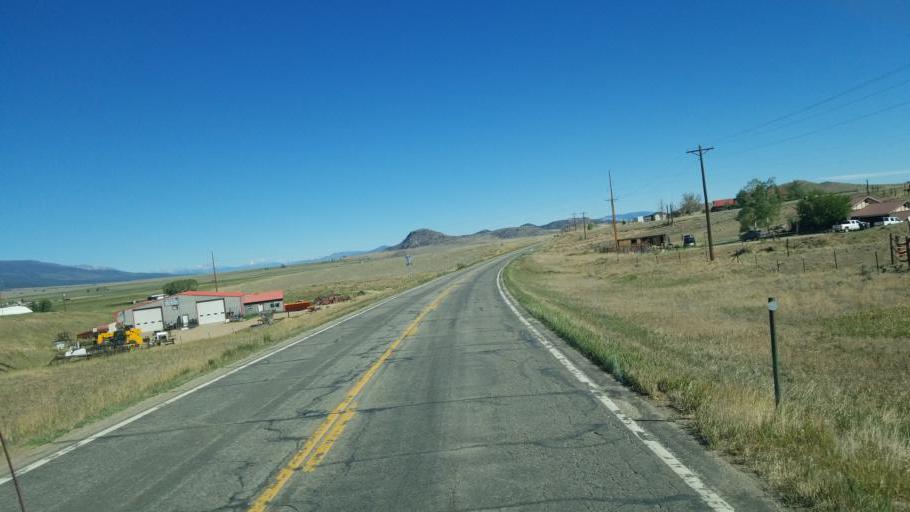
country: US
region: Colorado
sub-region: Custer County
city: Westcliffe
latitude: 38.1438
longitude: -105.4742
